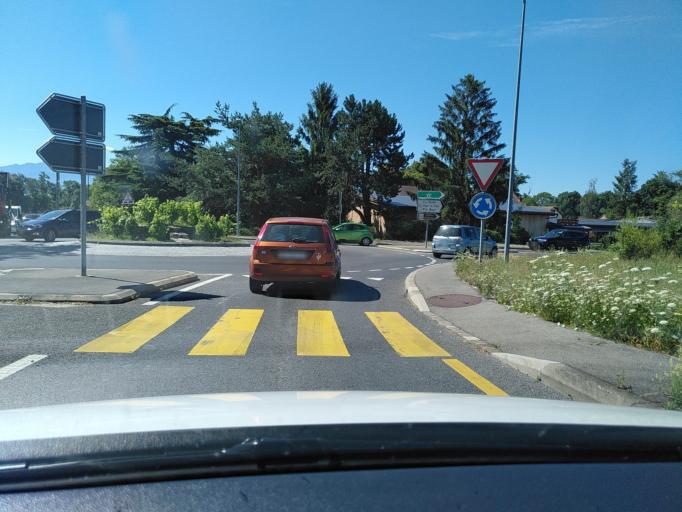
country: CH
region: Vaud
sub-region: Morges District
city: Aubonne
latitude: 46.4819
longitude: 6.4020
